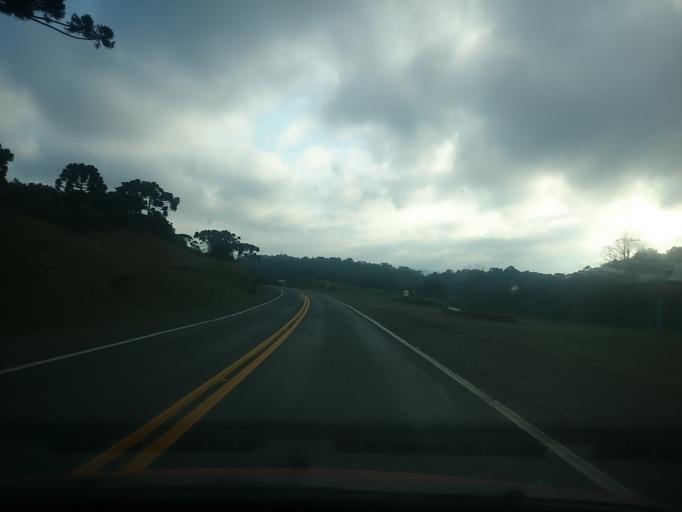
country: BR
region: Santa Catarina
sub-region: Lages
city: Lages
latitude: -28.0590
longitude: -50.5696
